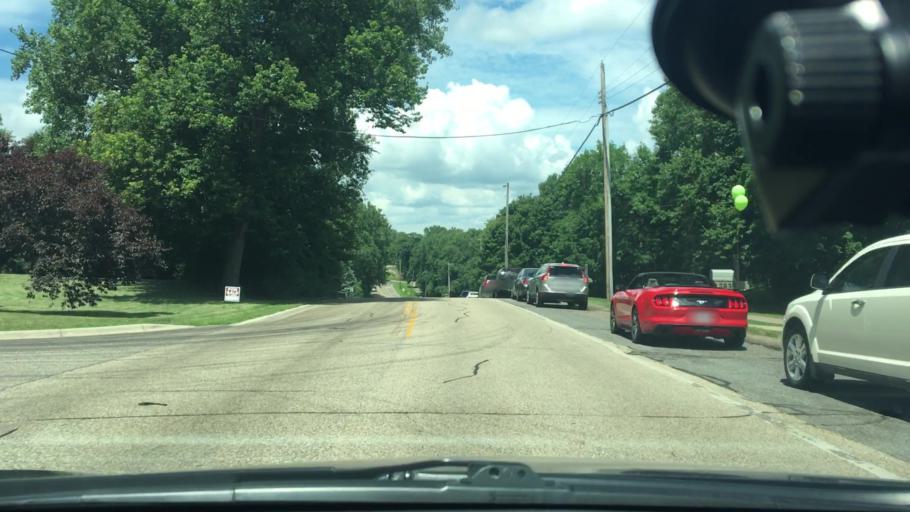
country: US
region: Minnesota
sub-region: Hennepin County
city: Plymouth
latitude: 45.0107
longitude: -93.4348
